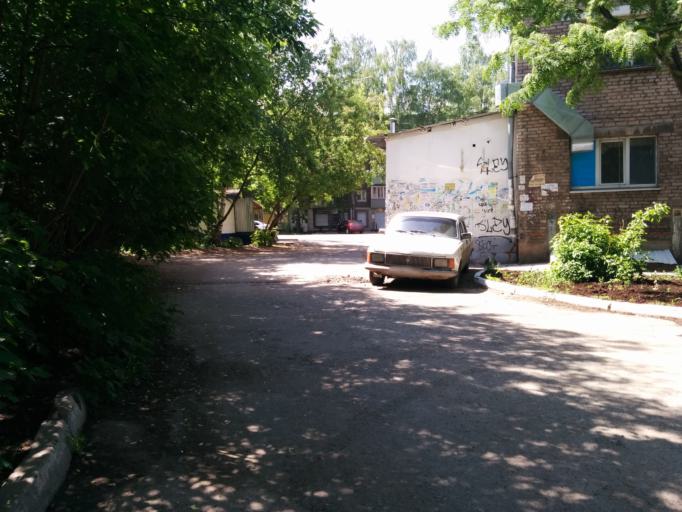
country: RU
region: Perm
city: Perm
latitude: 58.0186
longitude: 56.2924
